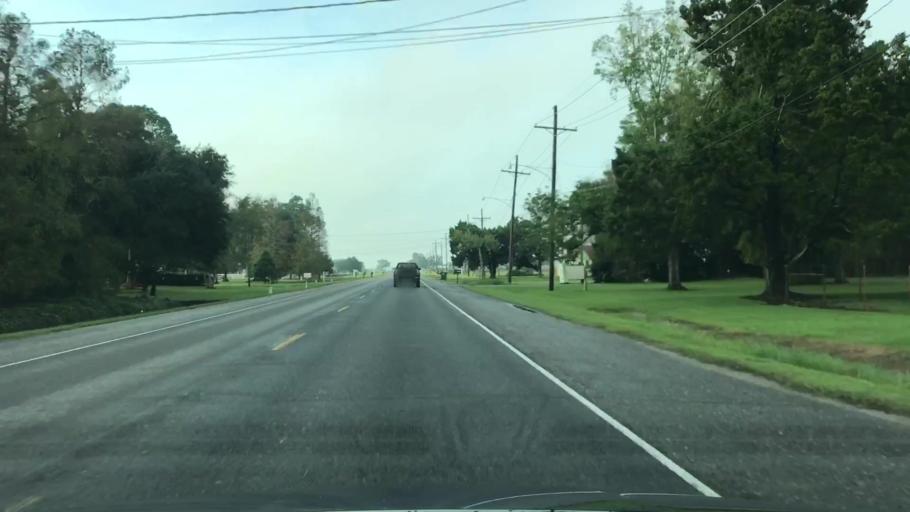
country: US
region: Louisiana
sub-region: Terrebonne Parish
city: Gray
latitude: 29.6707
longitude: -90.8165
